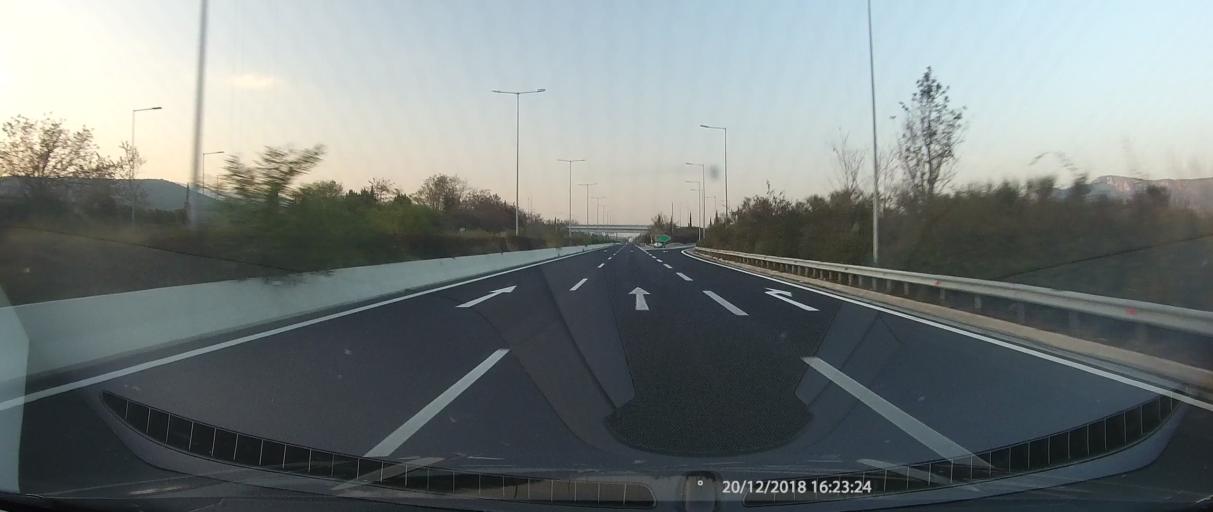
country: GR
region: Thessaly
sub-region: Nomos Magnisias
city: Sourpi
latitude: 39.0893
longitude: 22.8741
